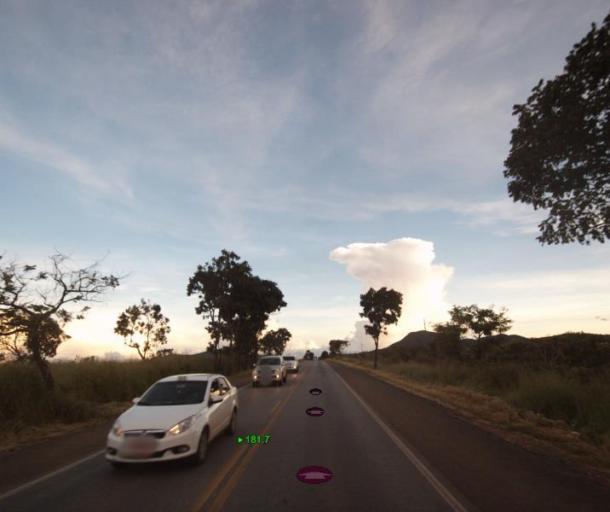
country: BR
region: Goias
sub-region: Uruacu
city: Uruacu
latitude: -14.3642
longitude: -49.1584
